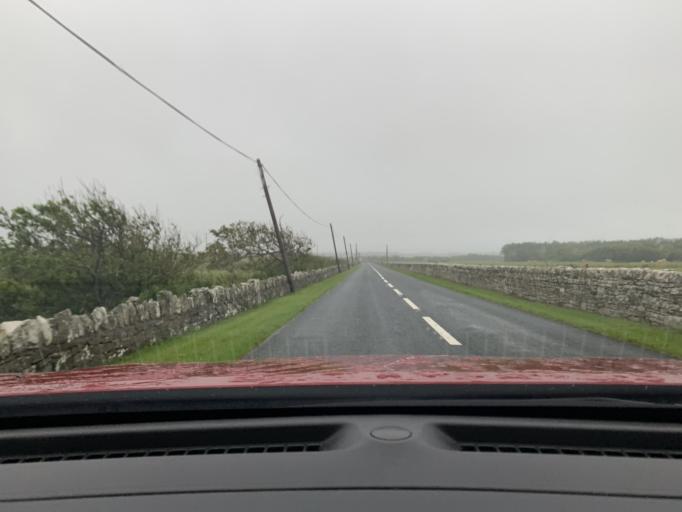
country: IE
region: Connaught
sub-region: County Leitrim
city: Kinlough
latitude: 54.4559
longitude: -8.4551
